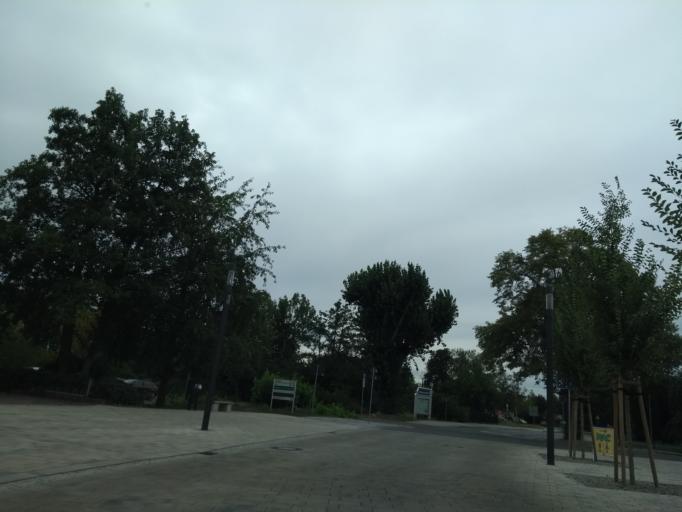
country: DE
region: Brandenburg
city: Lubbenau
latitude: 51.8620
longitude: 13.9676
